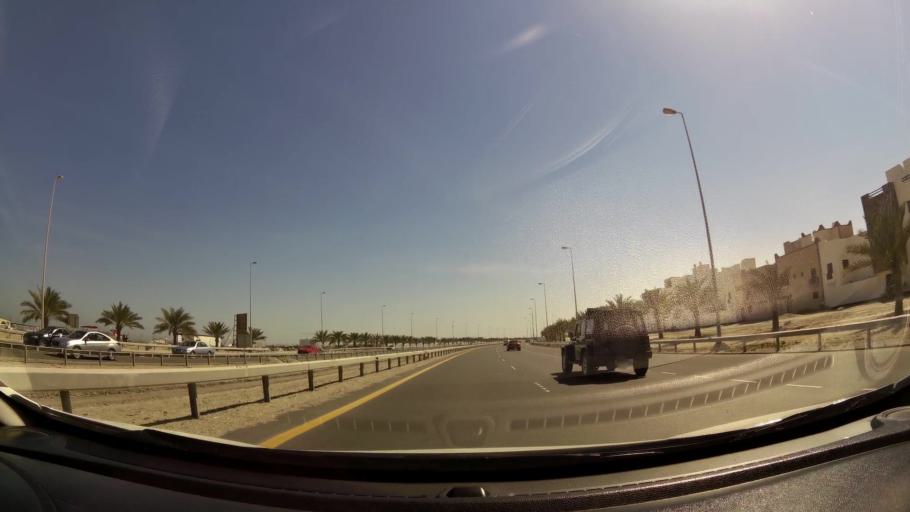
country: BH
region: Muharraq
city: Al Hadd
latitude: 26.2691
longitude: 50.6617
